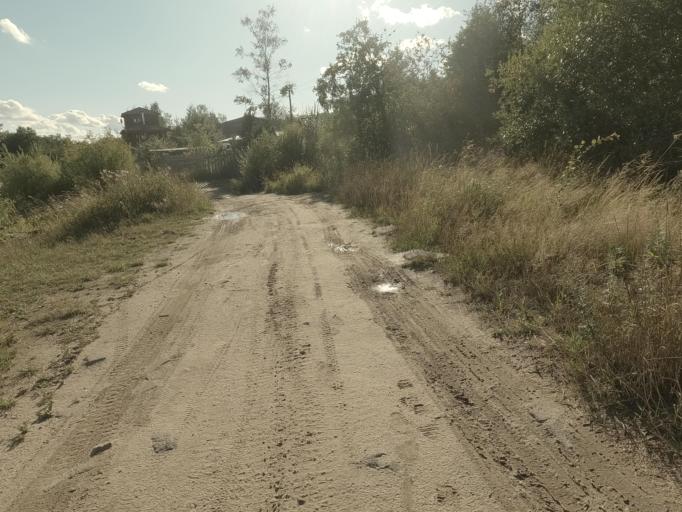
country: RU
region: Leningrad
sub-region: Volosovskiy Rayon
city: Shlissel'burg
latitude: 59.9443
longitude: 31.0039
